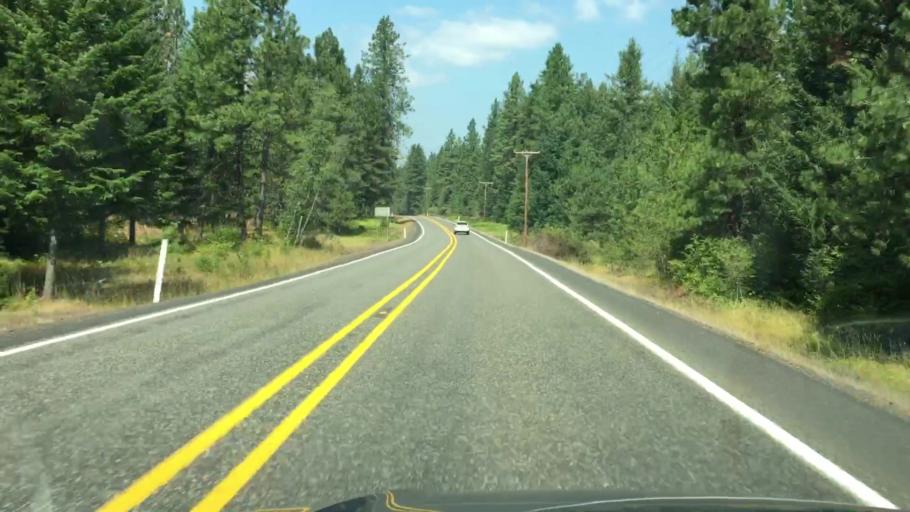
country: US
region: Washington
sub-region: Klickitat County
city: White Salmon
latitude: 45.9649
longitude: -121.4908
